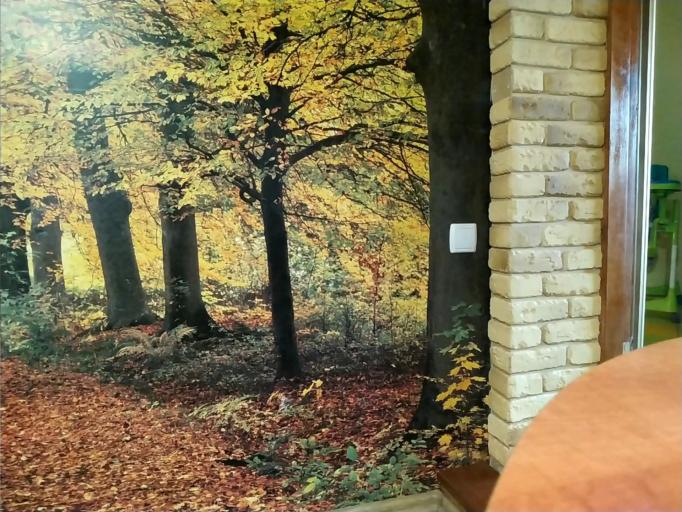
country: RU
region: Leningrad
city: Tolmachevo
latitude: 58.9287
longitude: 29.7256
